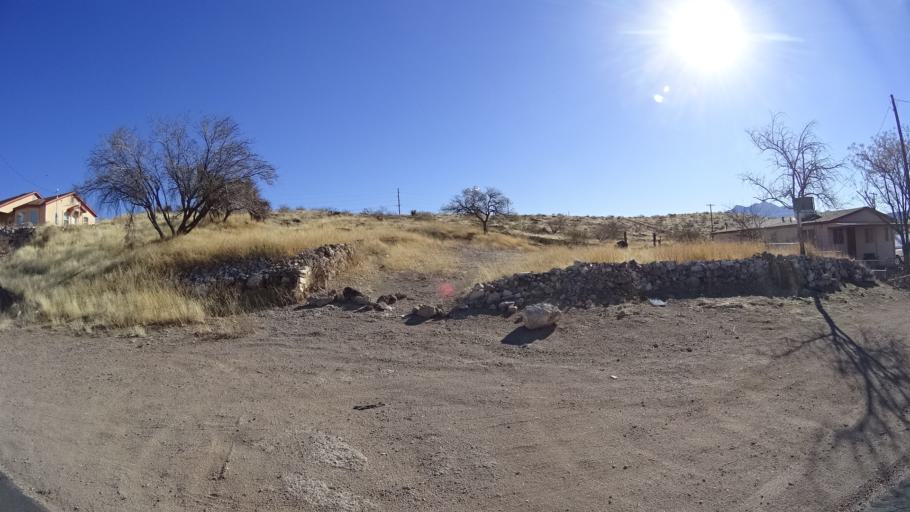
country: US
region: Arizona
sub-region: Mohave County
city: Kingman
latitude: 35.1839
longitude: -114.0491
